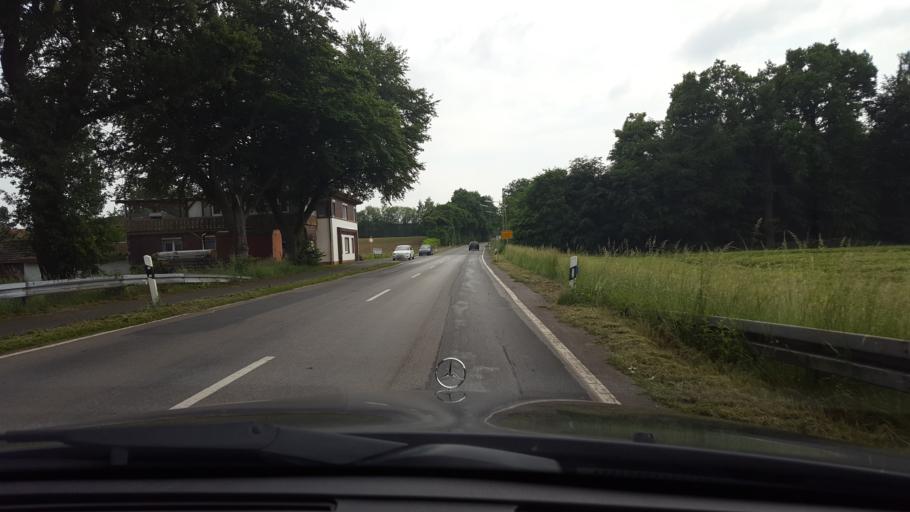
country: DE
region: North Rhine-Westphalia
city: Oer-Erkenschwick
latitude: 51.6536
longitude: 7.2758
